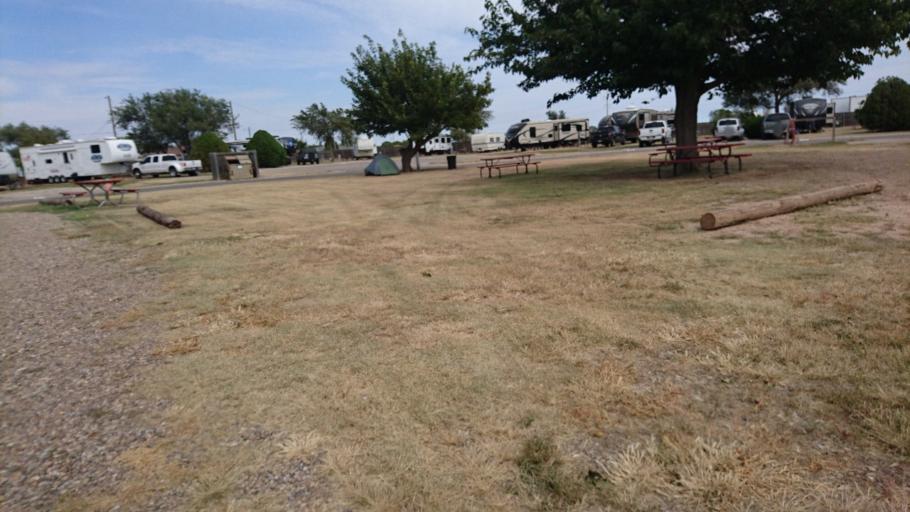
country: US
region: Texas
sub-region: Potter County
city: Amarillo
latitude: 35.1957
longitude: -101.7727
